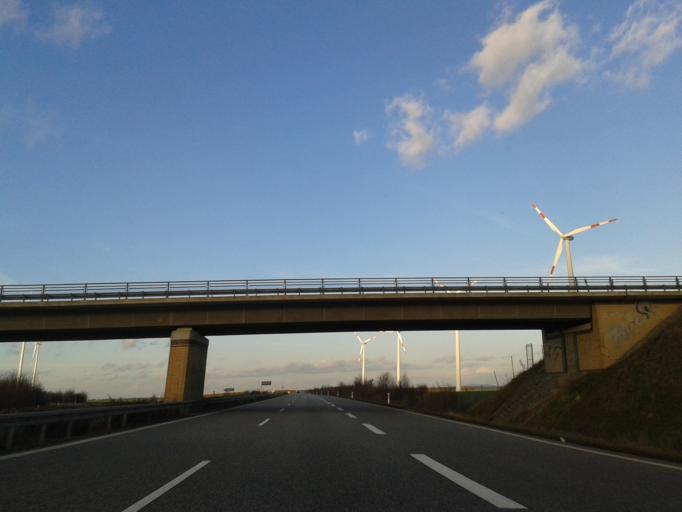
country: DE
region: Saxony-Anhalt
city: Holleben
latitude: 51.4262
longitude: 11.8643
